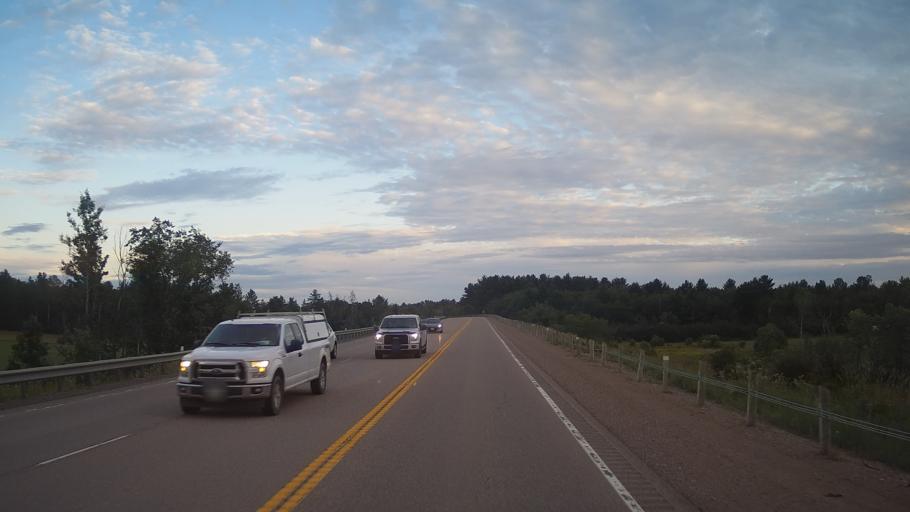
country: CA
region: Ontario
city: Pembroke
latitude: 45.8073
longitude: -77.2019
